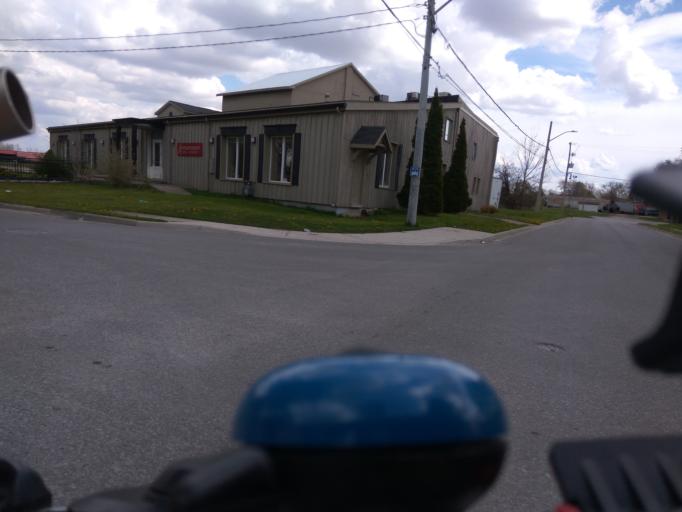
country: CA
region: Ontario
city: Stratford
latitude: 43.3656
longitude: -80.9736
